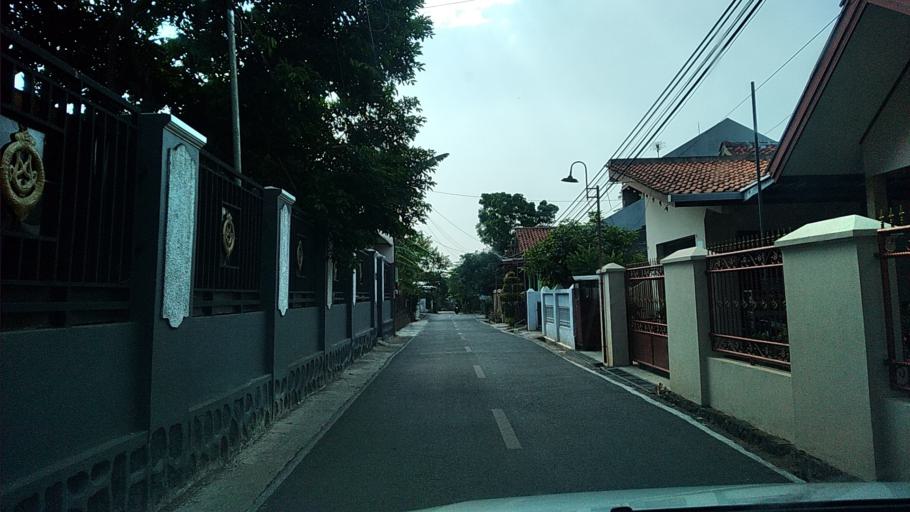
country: ID
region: Central Java
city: Ungaran
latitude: -7.0708
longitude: 110.4135
